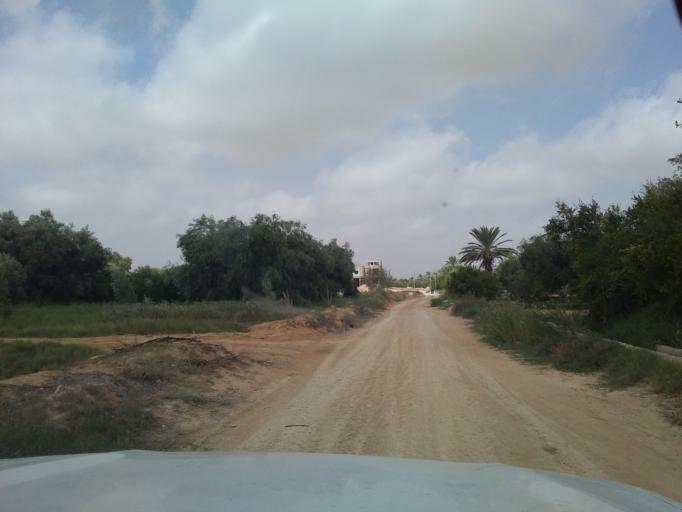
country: TN
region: Madanin
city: Medenine
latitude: 33.6226
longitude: 10.3145
